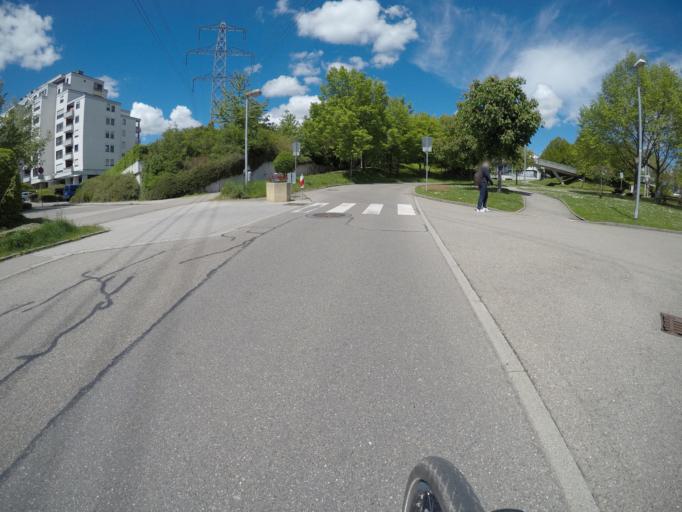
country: DE
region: Baden-Wuerttemberg
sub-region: Regierungsbezirk Stuttgart
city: Holzgerlingen
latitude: 48.6441
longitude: 9.0150
